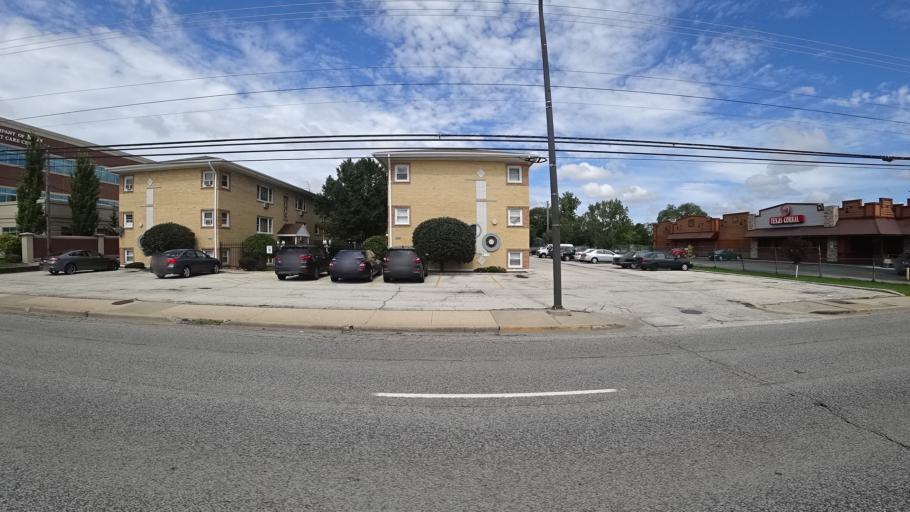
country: US
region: Illinois
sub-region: Cook County
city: Burbank
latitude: 41.7195
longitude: -87.7862
